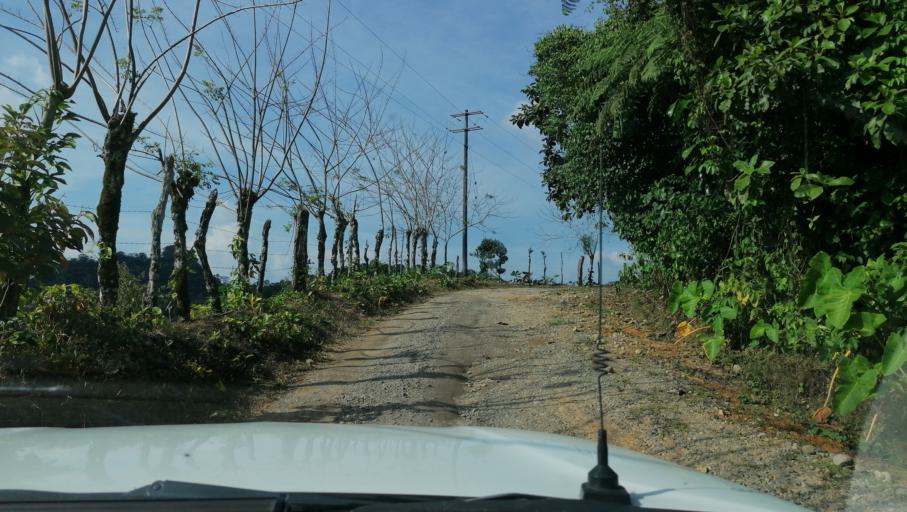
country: MX
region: Chiapas
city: Ostuacan
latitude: 17.4682
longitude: -93.2363
